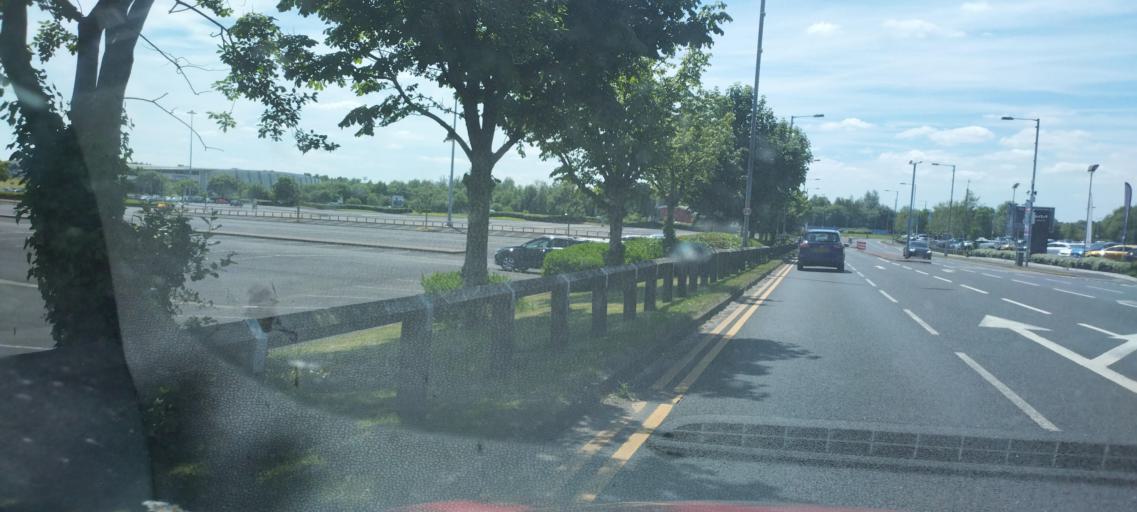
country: GB
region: England
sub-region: Borough of Bolton
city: Horwich
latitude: 53.5837
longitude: -2.5387
